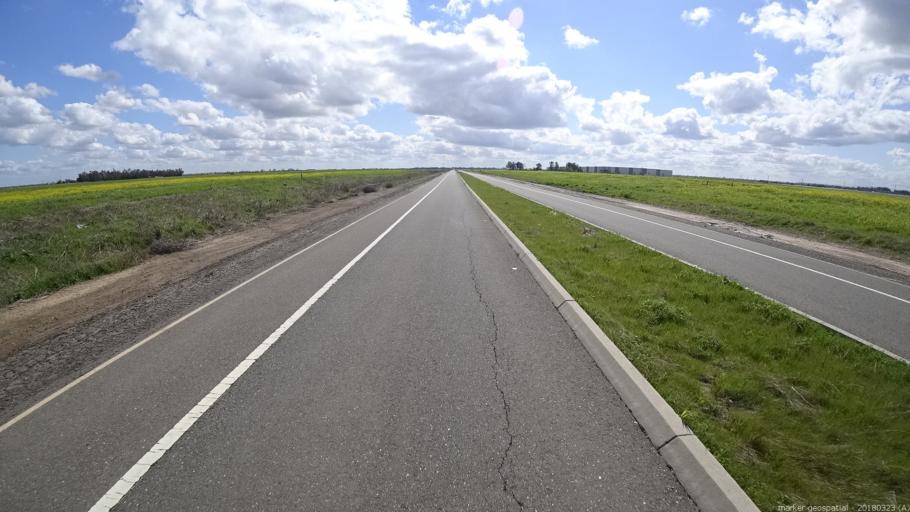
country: US
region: California
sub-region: Sacramento County
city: Elverta
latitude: 38.6914
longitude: -121.5696
